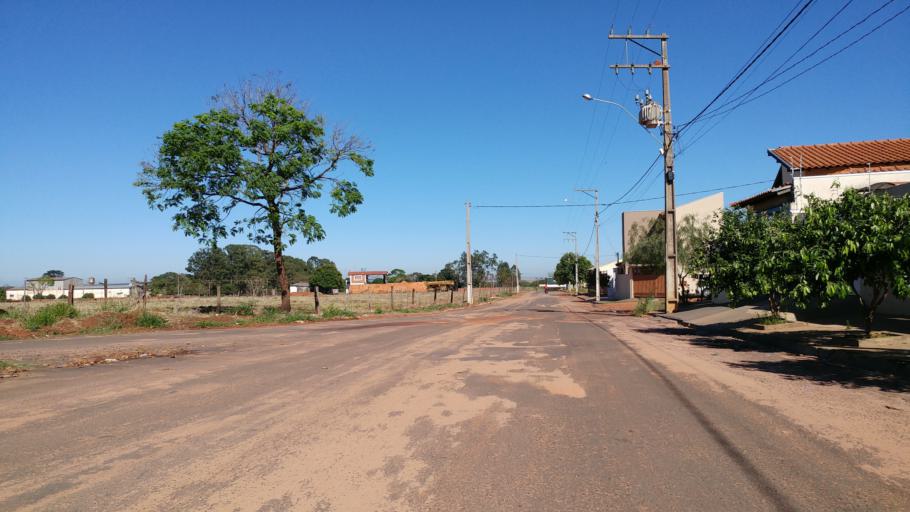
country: BR
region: Sao Paulo
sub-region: Paraguacu Paulista
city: Paraguacu Paulista
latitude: -22.4178
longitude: -50.5903
